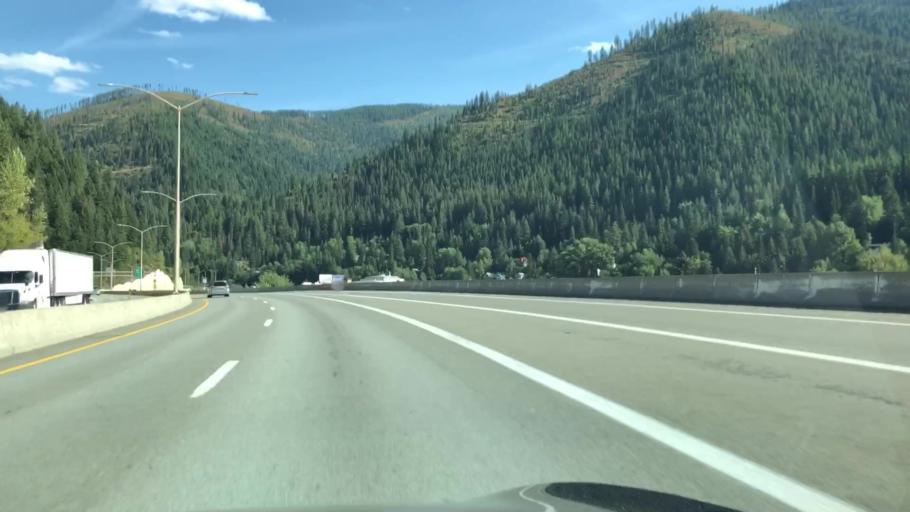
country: US
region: Idaho
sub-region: Shoshone County
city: Wallace
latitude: 47.4755
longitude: -115.9286
